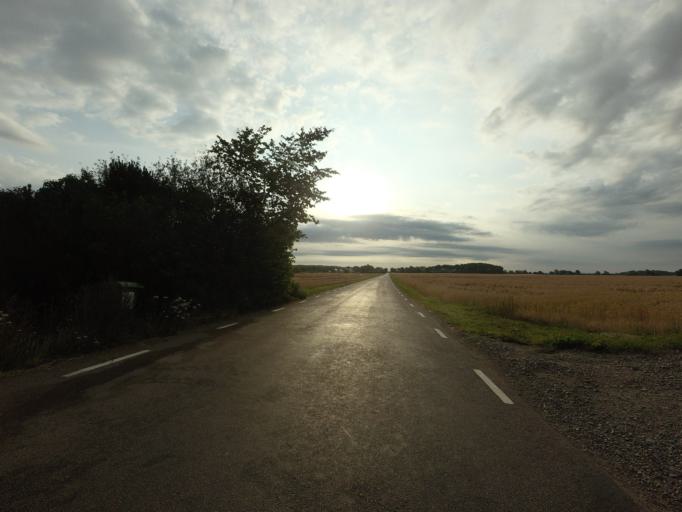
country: SE
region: Skane
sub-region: Helsingborg
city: Odakra
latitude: 56.1535
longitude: 12.6794
